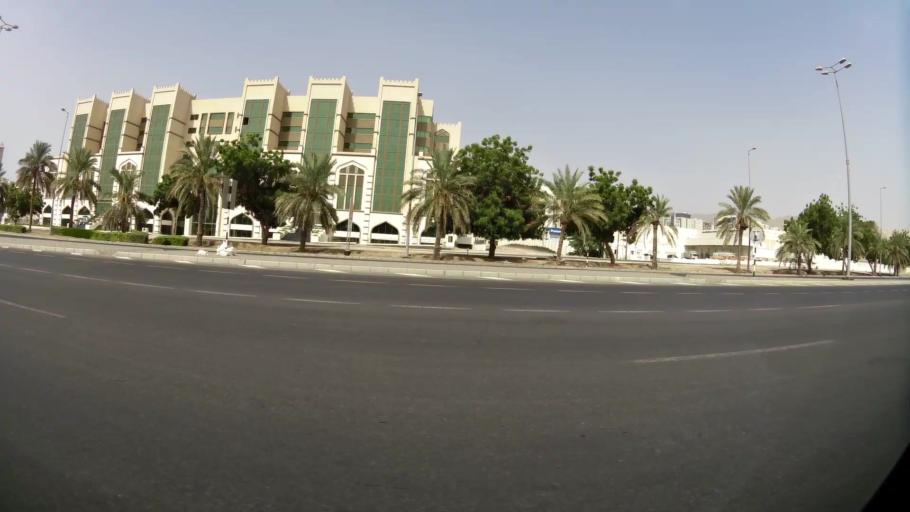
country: OM
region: Muhafazat Masqat
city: Bawshar
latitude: 23.5789
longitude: 58.4079
